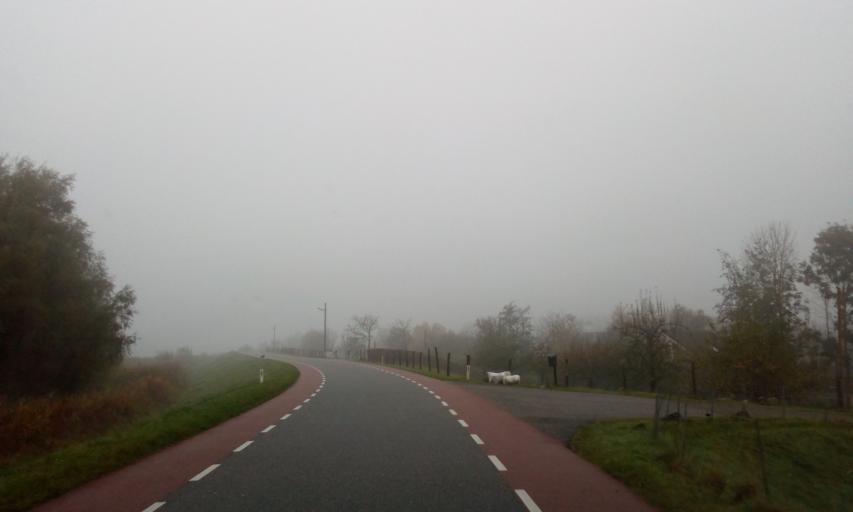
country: NL
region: South Holland
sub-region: Molenwaard
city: Nieuw-Lekkerland
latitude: 51.9155
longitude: 4.7570
